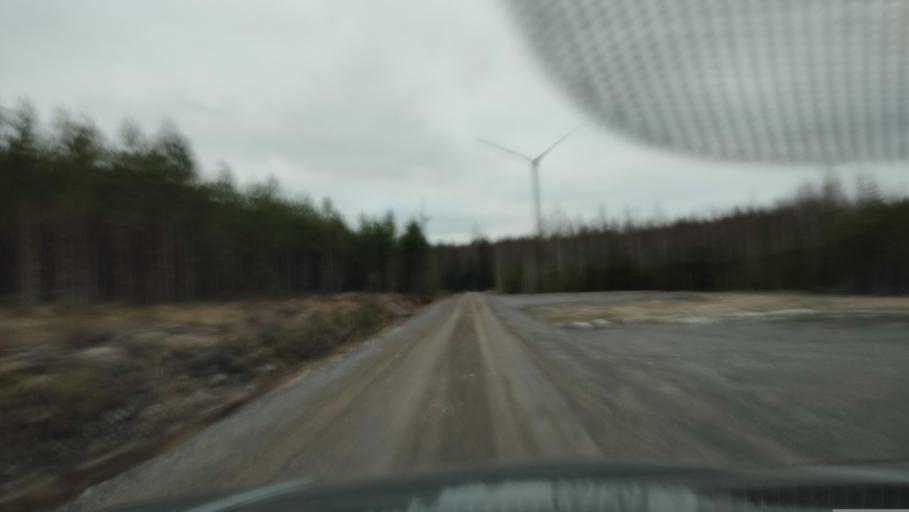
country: FI
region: Southern Ostrobothnia
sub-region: Suupohja
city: Karijoki
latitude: 62.2084
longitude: 21.5999
